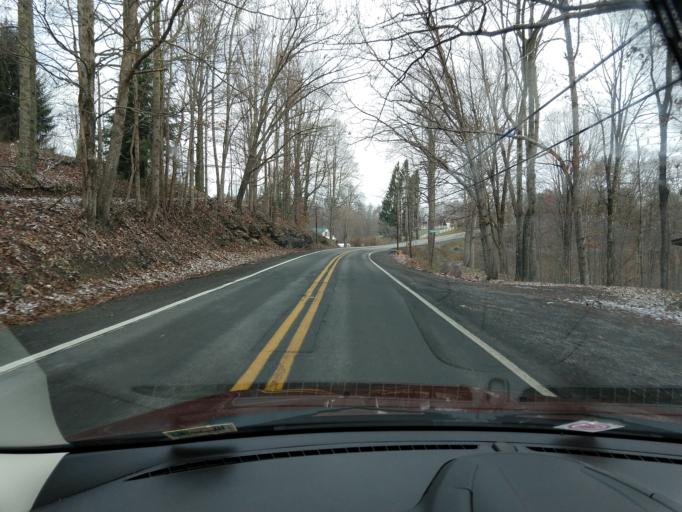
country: US
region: West Virginia
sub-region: Nicholas County
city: Craigsville
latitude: 38.2064
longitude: -80.6825
